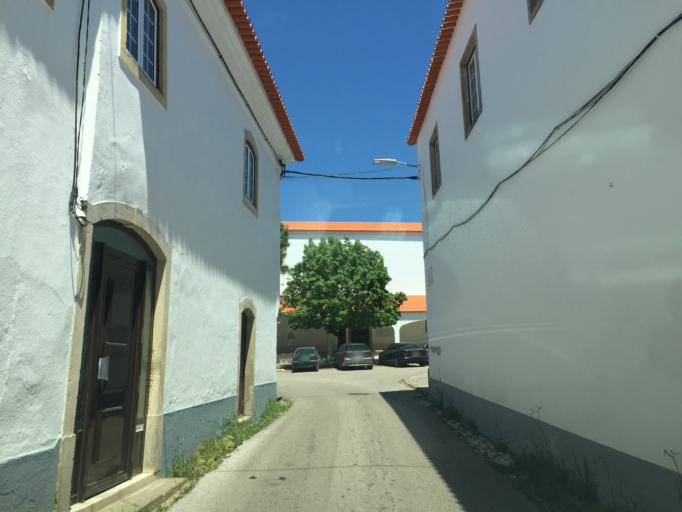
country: PT
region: Santarem
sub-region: Ferreira do Zezere
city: Ferreira do Zezere
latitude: 39.5996
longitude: -8.3009
